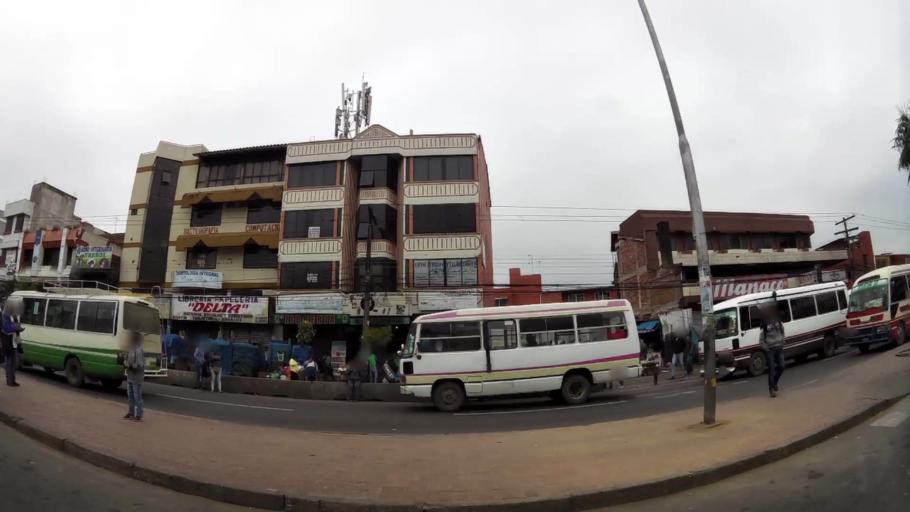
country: BO
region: Santa Cruz
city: Santa Cruz de la Sierra
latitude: -17.7956
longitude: -63.1899
